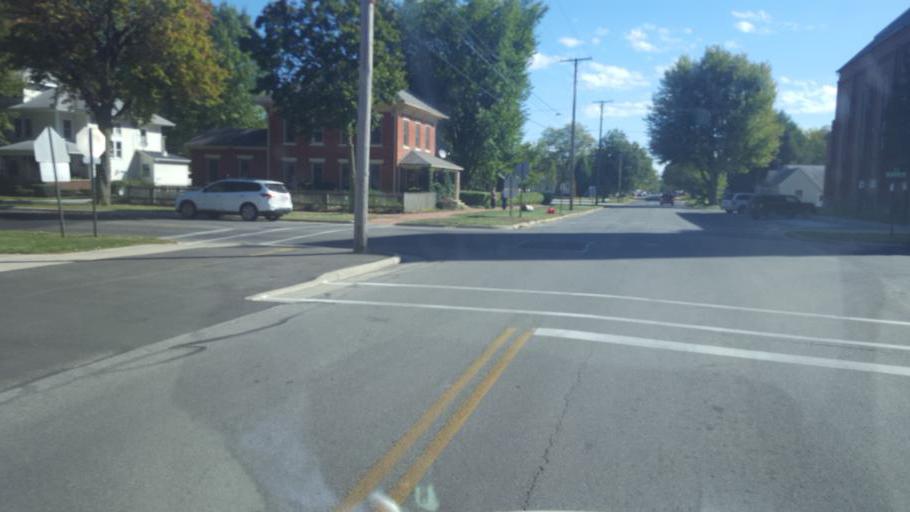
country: US
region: Ohio
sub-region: Wyandot County
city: Upper Sandusky
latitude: 40.8303
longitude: -83.2847
